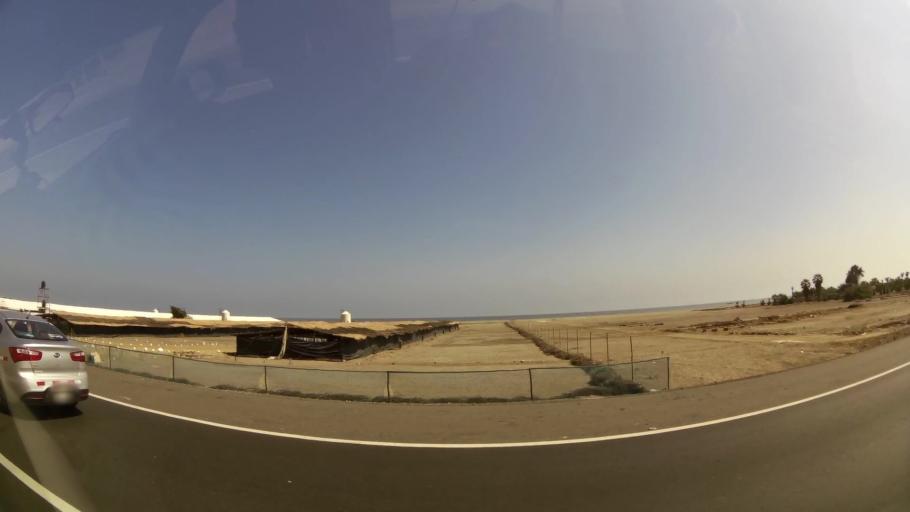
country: PE
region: Ica
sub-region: Provincia de Chincha
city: San Pedro
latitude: -13.3765
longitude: -76.2079
